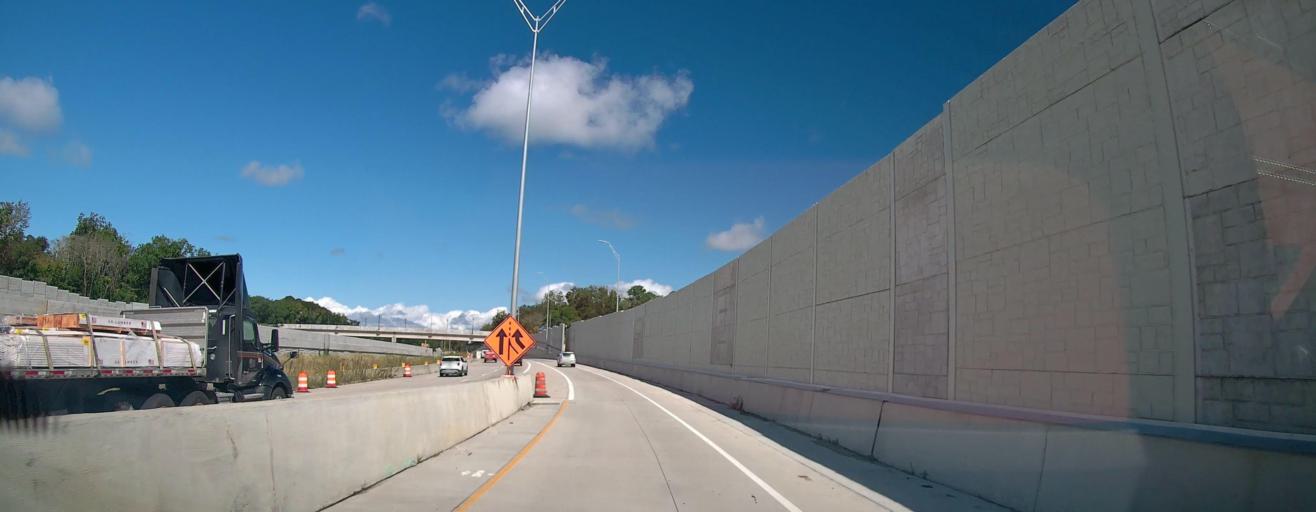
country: US
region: Georgia
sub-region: Bibb County
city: Macon
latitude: 32.8450
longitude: -83.6422
